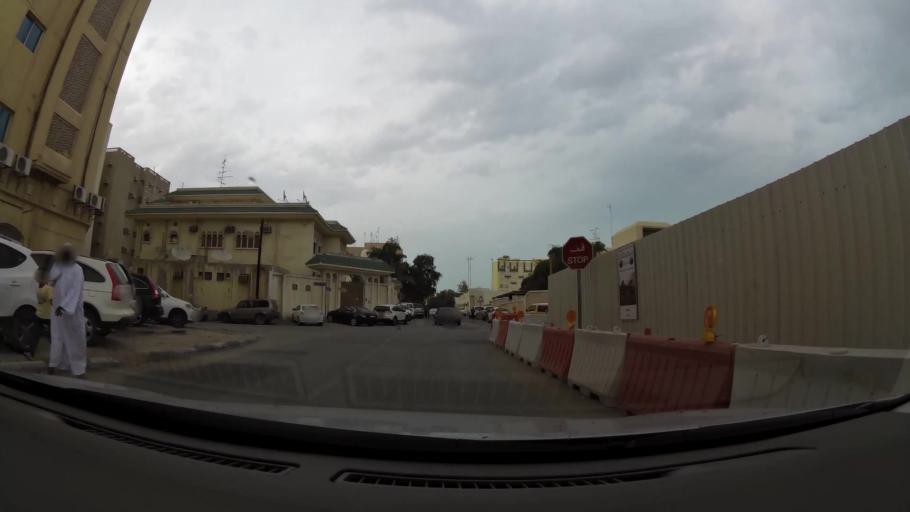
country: QA
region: Baladiyat ad Dawhah
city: Doha
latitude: 25.2866
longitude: 51.5098
